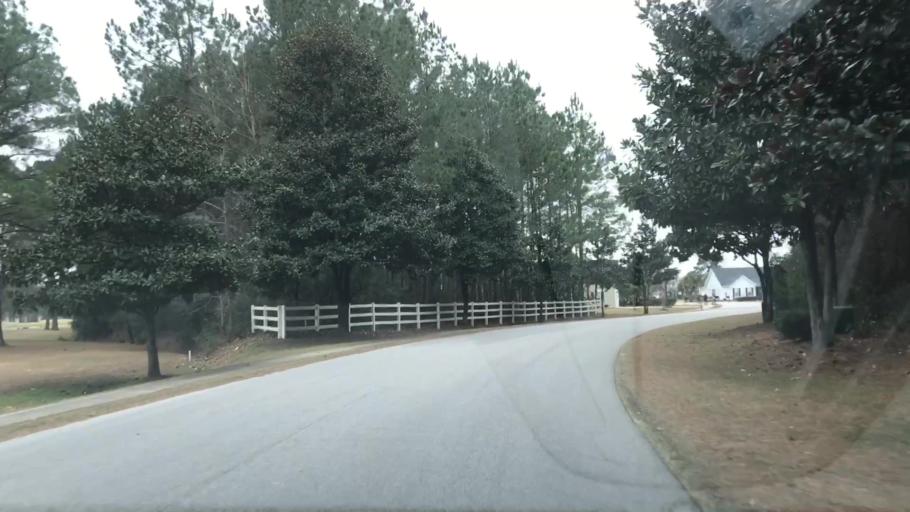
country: US
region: South Carolina
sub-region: Horry County
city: Red Hill
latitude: 33.7732
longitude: -79.0043
